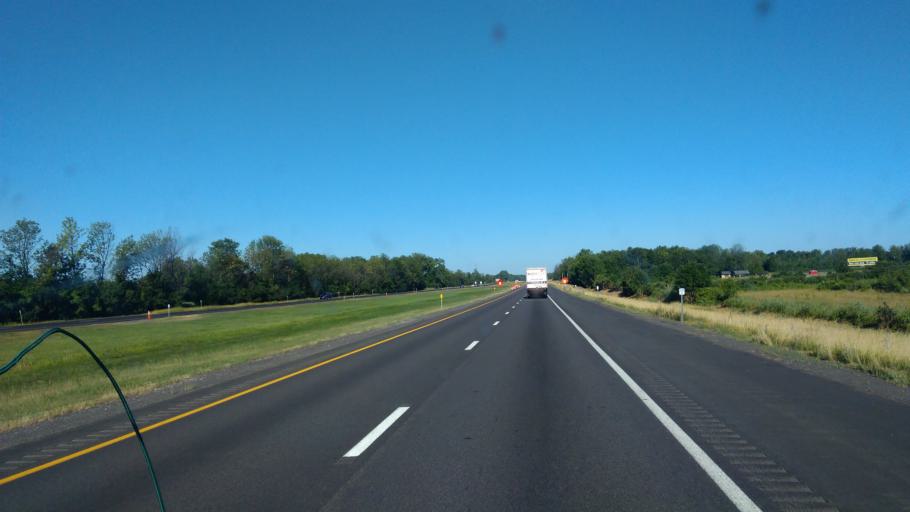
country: US
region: New York
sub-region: Ontario County
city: Clifton Springs
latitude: 42.9742
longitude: -77.1157
